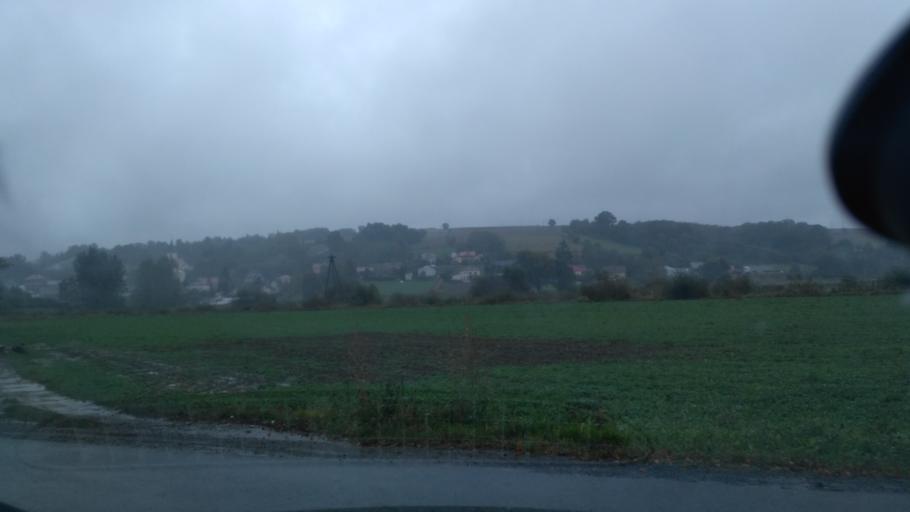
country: PL
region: Subcarpathian Voivodeship
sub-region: Powiat ropczycko-sedziszowski
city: Niedzwiada
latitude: 49.9951
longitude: 21.5554
